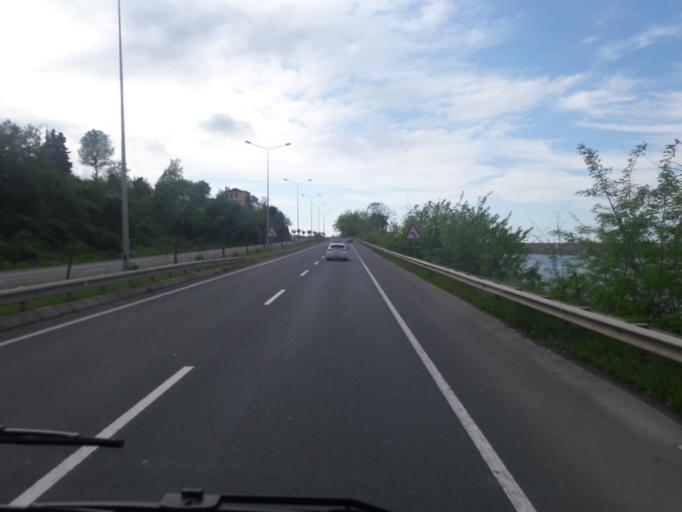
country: TR
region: Giresun
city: Piraziz
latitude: 40.9600
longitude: 38.1063
